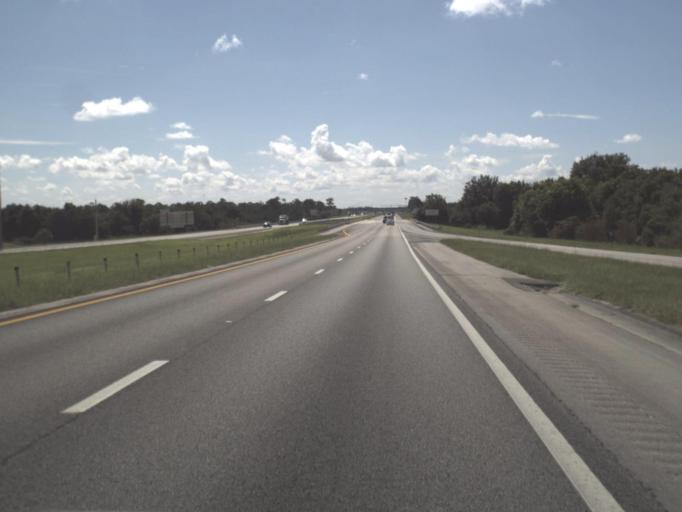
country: US
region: Florida
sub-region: Charlotte County
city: Charlotte Park
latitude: 26.8931
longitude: -82.0005
